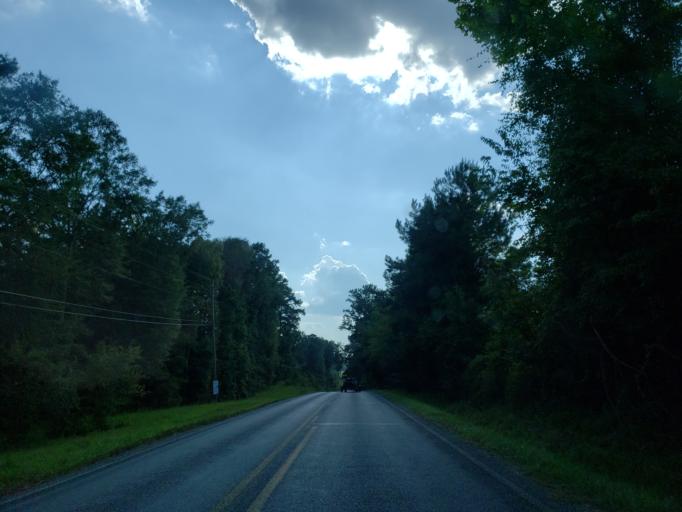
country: US
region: Mississippi
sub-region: Jones County
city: Sharon
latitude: 31.9197
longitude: -89.0243
